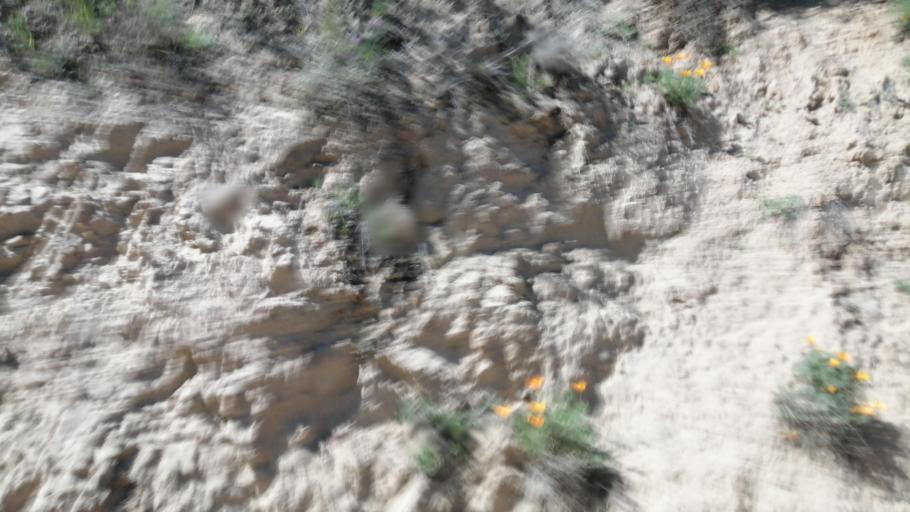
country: CL
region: Valparaiso
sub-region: Provincia de Marga Marga
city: Limache
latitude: -33.1999
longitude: -71.2621
